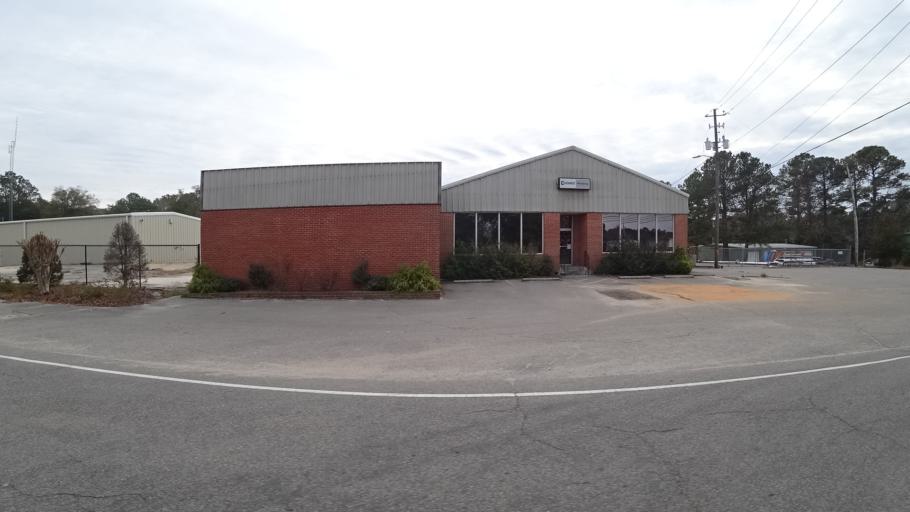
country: US
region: North Carolina
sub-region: Moore County
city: Pinehurst
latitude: 35.2006
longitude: -79.4683
